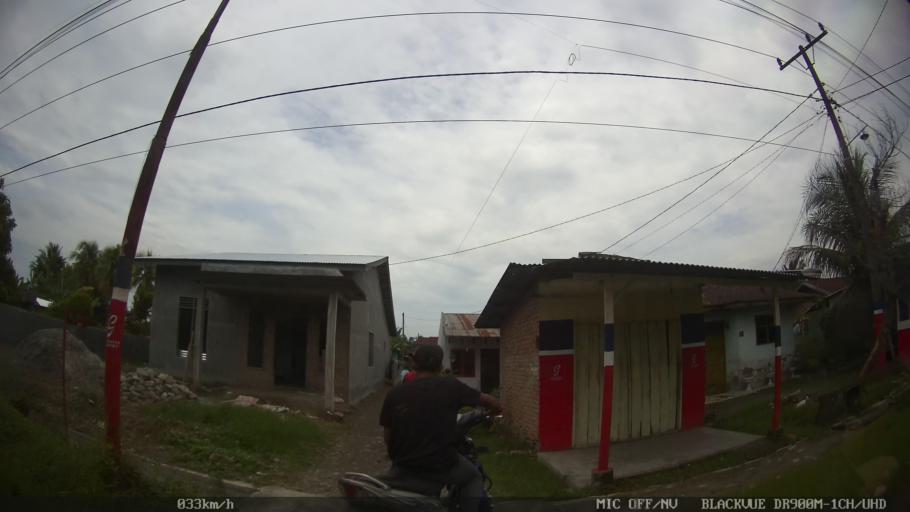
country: ID
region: North Sumatra
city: Binjai
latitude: 3.6384
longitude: 98.5525
